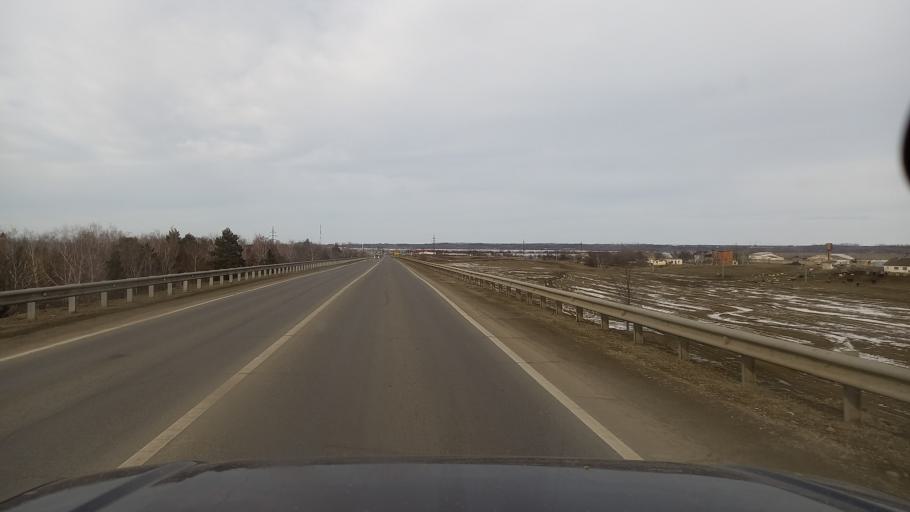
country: RU
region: Krasnodarskiy
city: Belorechensk
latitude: 44.7621
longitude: 39.9151
